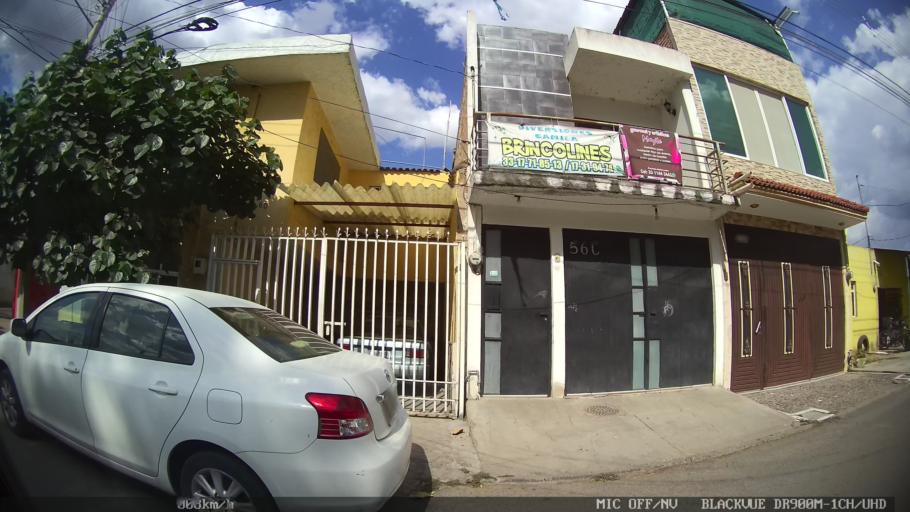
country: MX
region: Jalisco
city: Tlaquepaque
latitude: 20.6602
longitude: -103.2628
